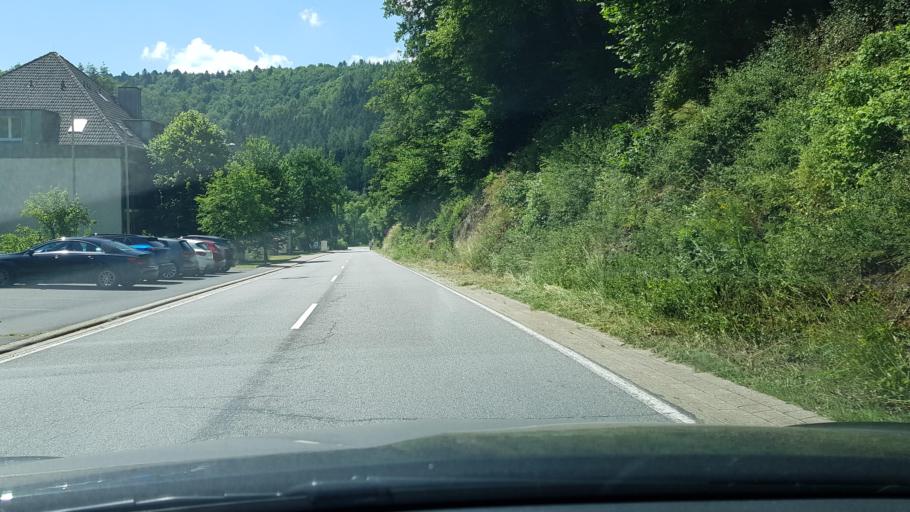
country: DE
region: Rheinland-Pfalz
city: Volkesfeld
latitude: 50.3856
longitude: 7.1539
